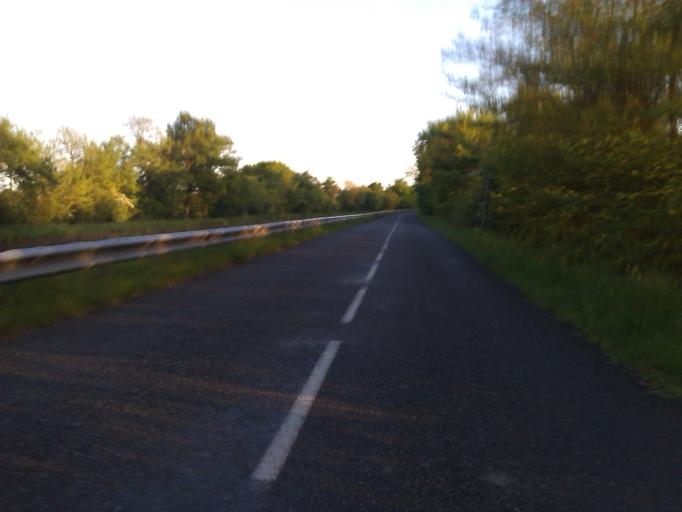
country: FR
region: Bourgogne
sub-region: Departement de Saone-et-Loire
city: Paray-le-Monial
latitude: 46.4756
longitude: 4.1722
